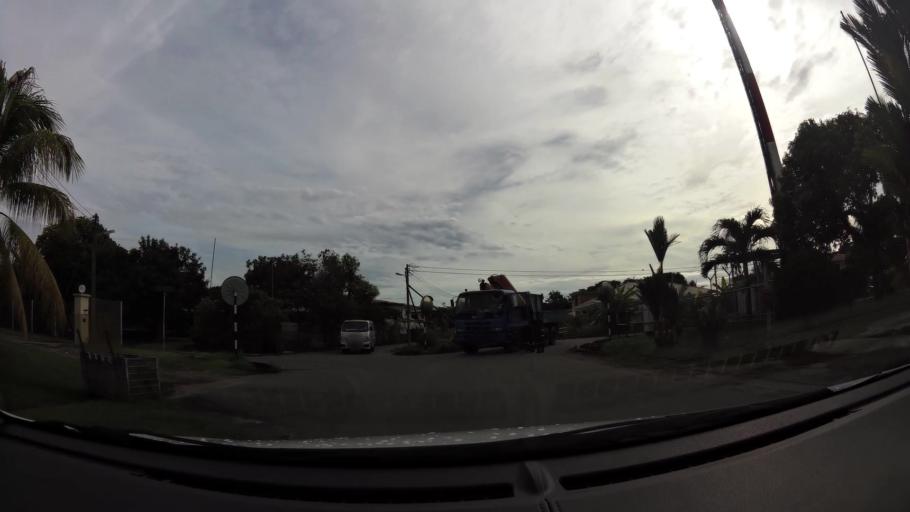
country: BN
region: Belait
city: Seria
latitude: 4.6140
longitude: 114.3575
